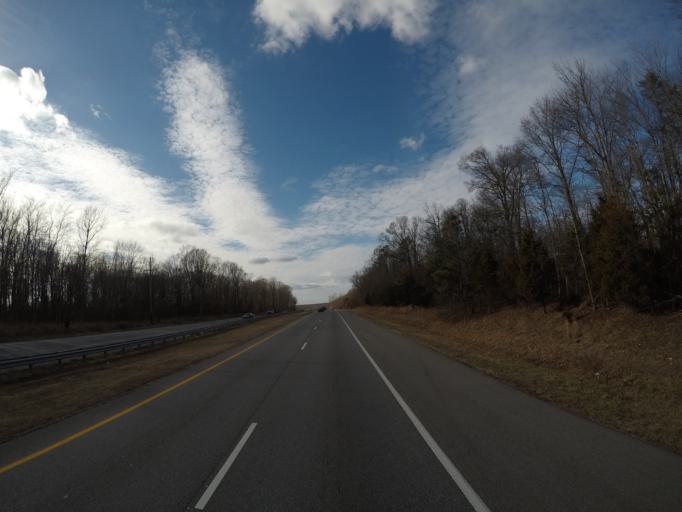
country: US
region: Maryland
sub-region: Charles County
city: Waldorf
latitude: 38.6511
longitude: -76.9646
